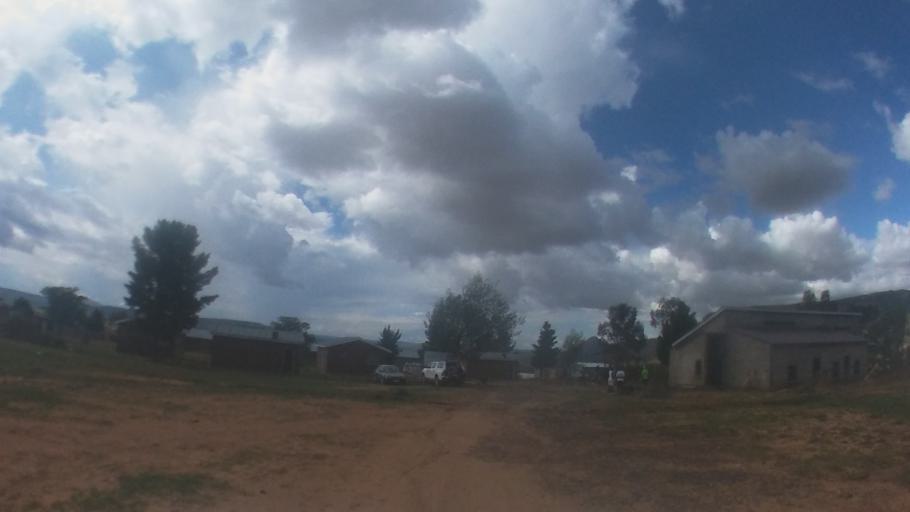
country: LS
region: Maseru
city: Maseru
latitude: -29.4406
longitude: 27.4128
